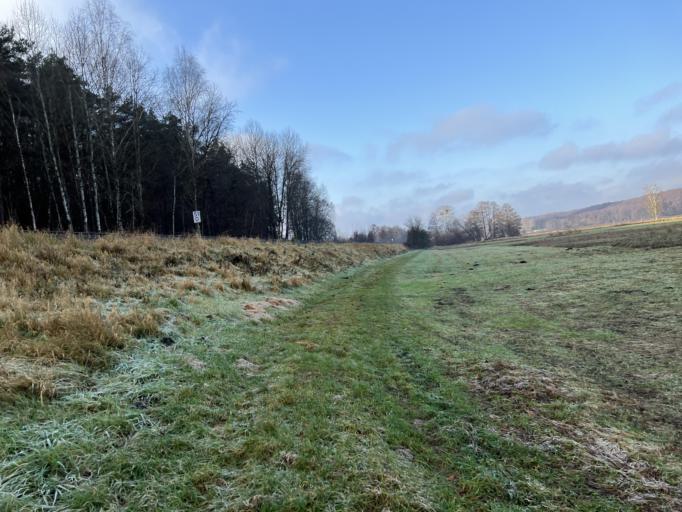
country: DE
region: Brandenburg
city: Eberswalde
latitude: 52.8425
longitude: 13.8726
